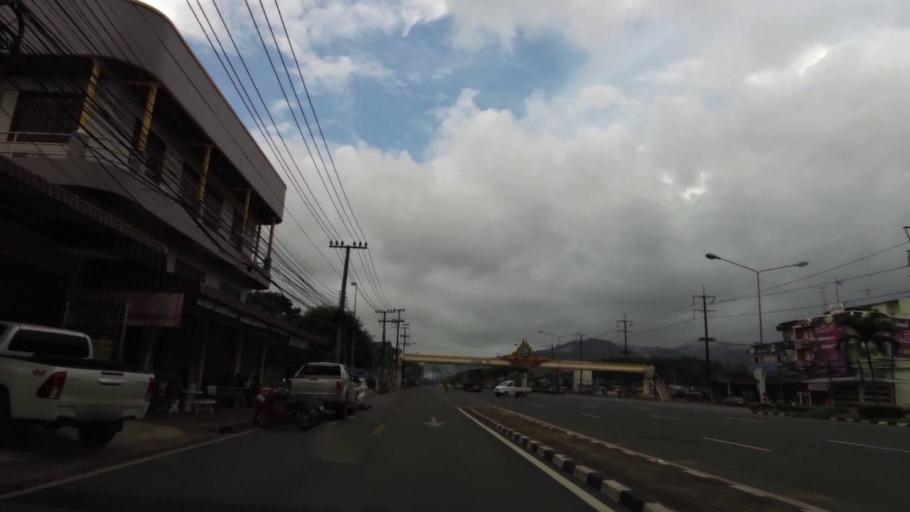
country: TH
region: Chanthaburi
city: Khlung
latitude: 12.4614
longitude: 102.2278
